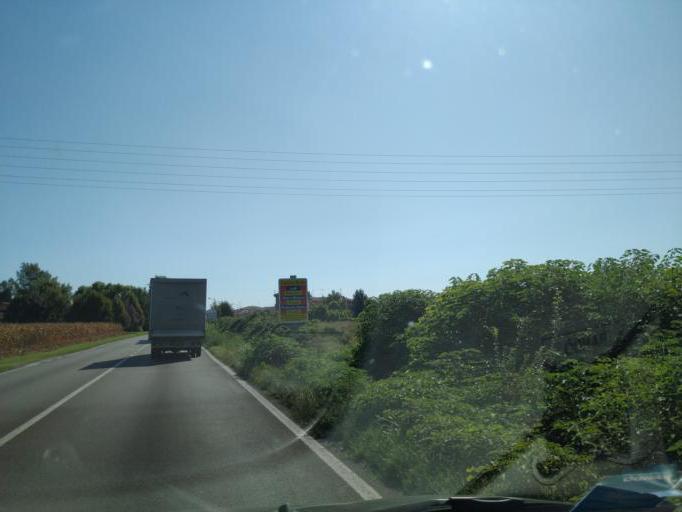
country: IT
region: Emilia-Romagna
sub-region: Provincia di Ferrara
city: Dosso
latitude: 44.7688
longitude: 11.3289
